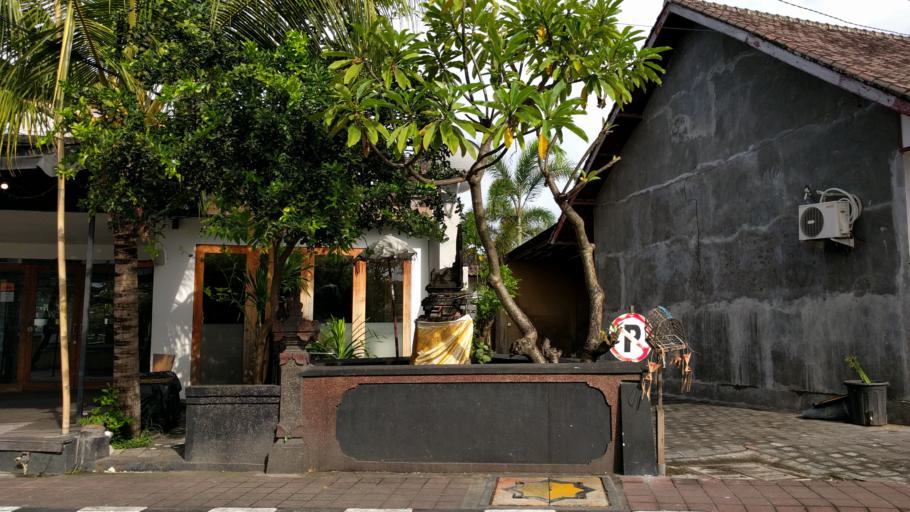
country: ID
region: Bali
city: Kuta
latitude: -8.6860
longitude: 115.1559
